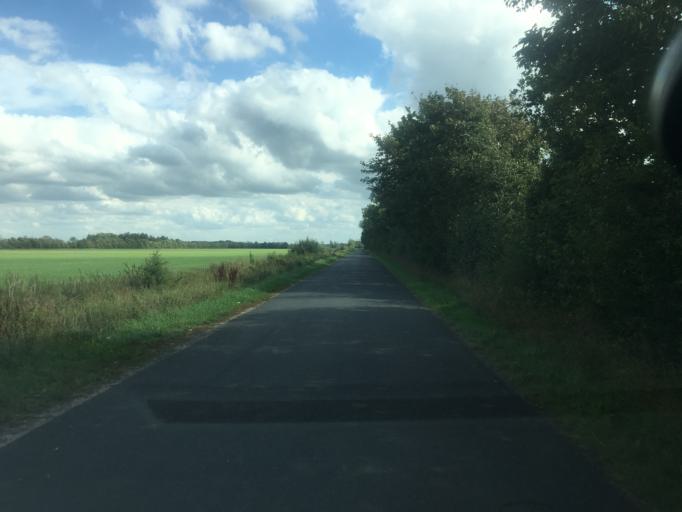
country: DK
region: South Denmark
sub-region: Tonder Kommune
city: Logumkloster
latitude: 55.0088
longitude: 9.0062
